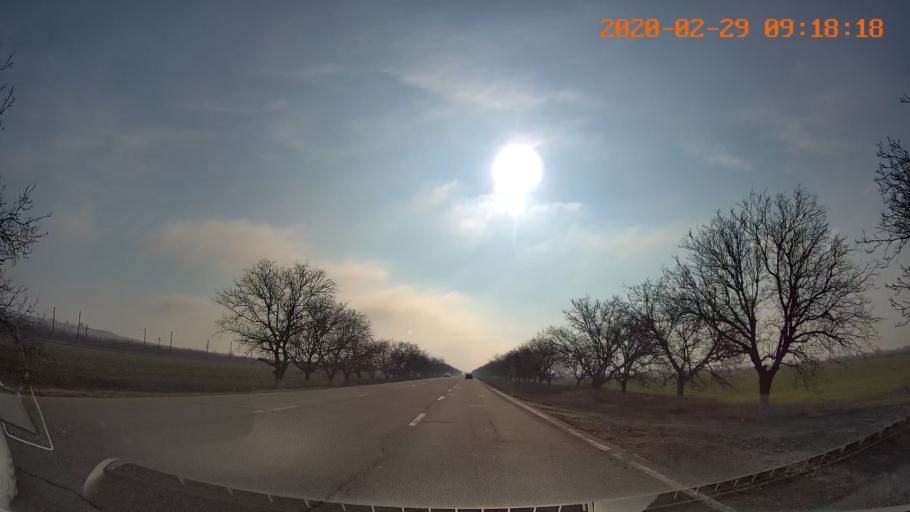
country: MD
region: Telenesti
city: Pervomaisc
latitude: 46.7749
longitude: 29.9203
